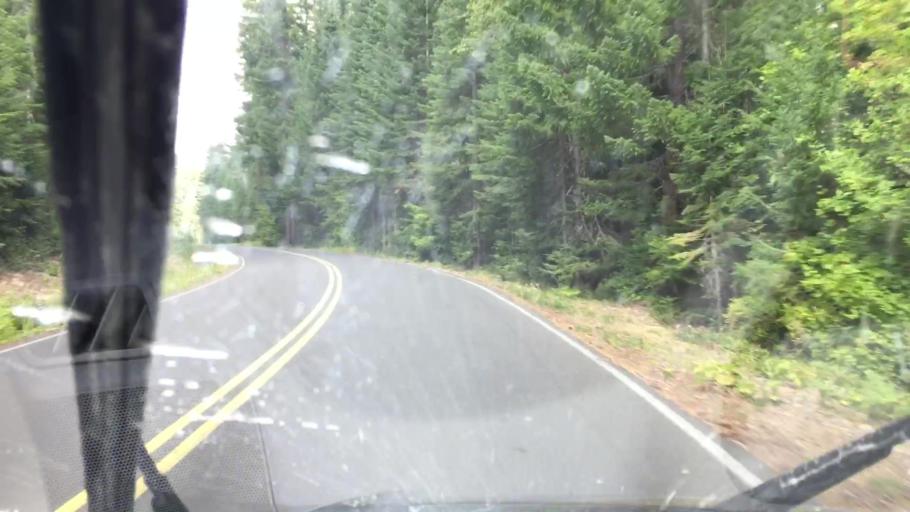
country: US
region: Washington
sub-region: Klickitat County
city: White Salmon
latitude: 46.0934
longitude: -121.6063
